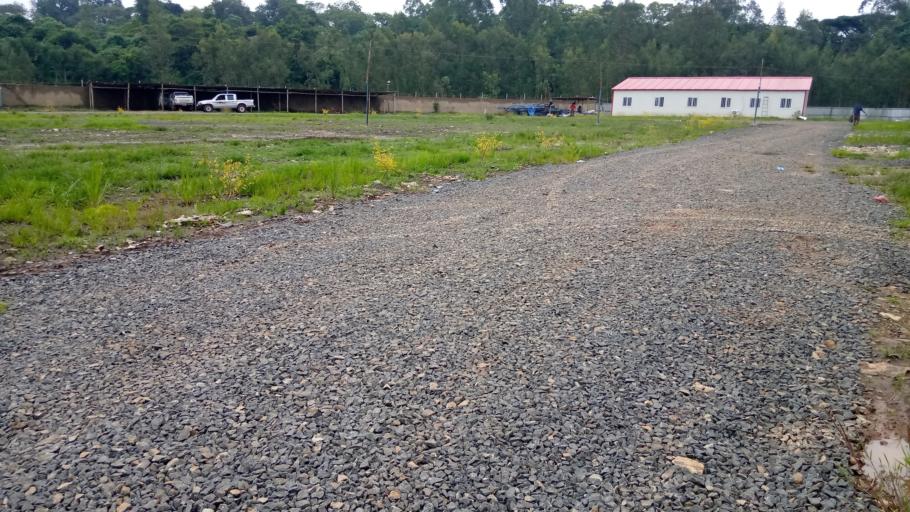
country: ET
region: Oromiya
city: Agaro
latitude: 7.8641
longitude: 36.6585
